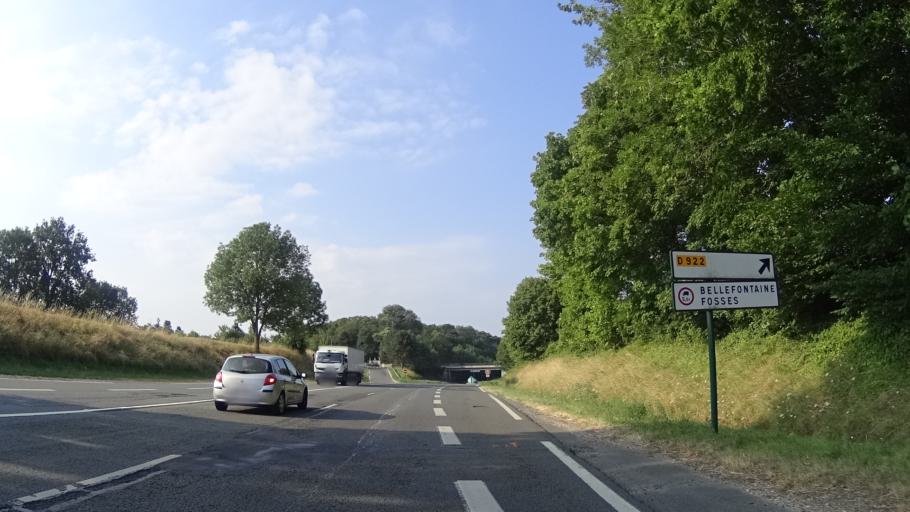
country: FR
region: Ile-de-France
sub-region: Departement du Val-d'Oise
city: Luzarches
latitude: 49.1128
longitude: 2.4305
